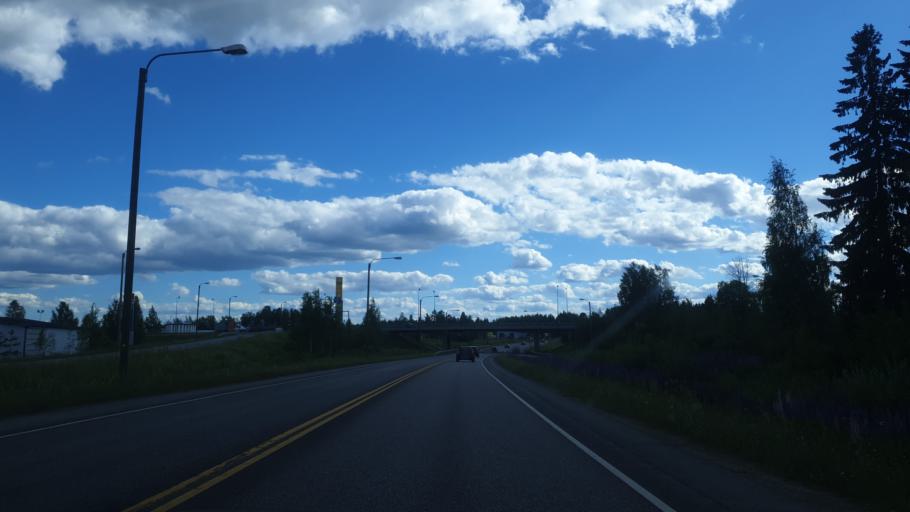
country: FI
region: Southern Savonia
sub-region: Pieksaemaeki
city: Juva
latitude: 61.9005
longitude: 27.8038
